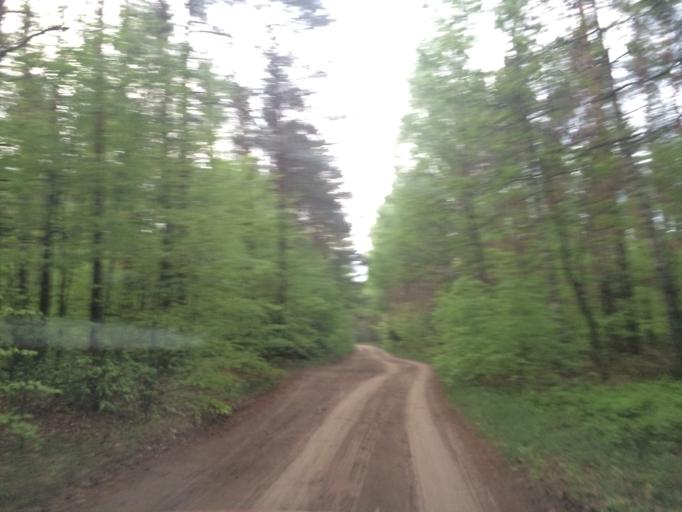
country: PL
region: Warmian-Masurian Voivodeship
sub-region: Powiat nowomiejski
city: Kurzetnik
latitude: 53.3565
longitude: 19.5179
